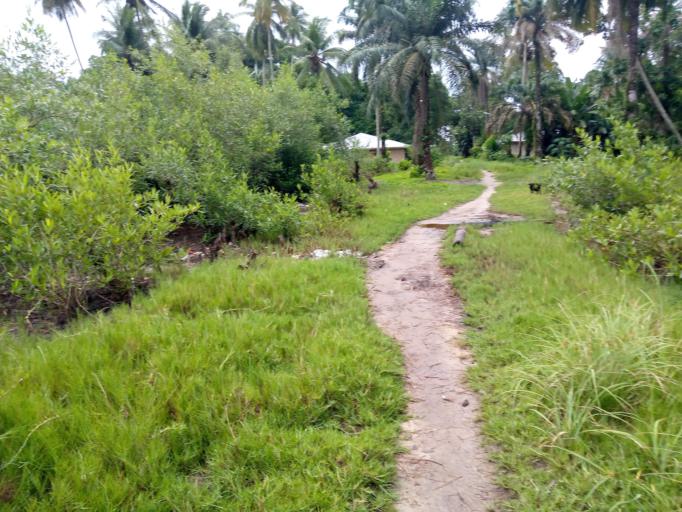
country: SL
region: Southern Province
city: Bonthe
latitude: 7.5330
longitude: -12.5055
